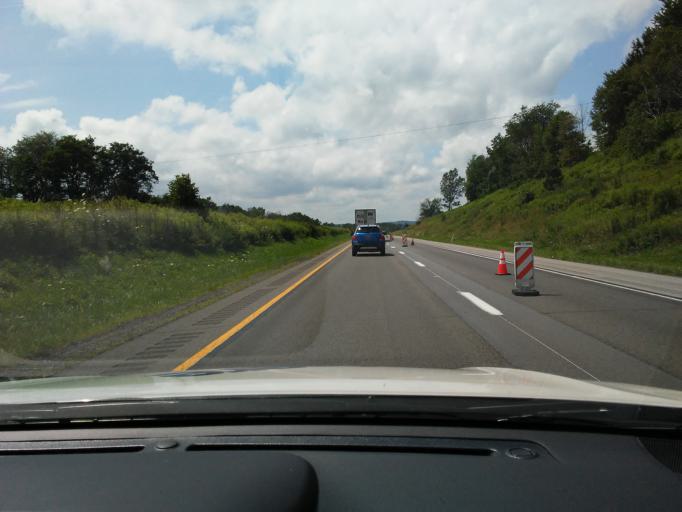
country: US
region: Pennsylvania
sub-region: Venango County
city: Seneca
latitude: 41.1760
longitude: -79.7536
